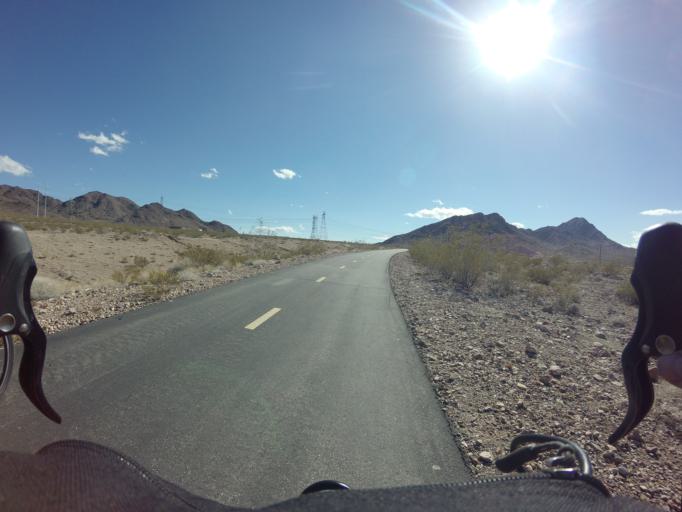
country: US
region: Nevada
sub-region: Clark County
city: Henderson
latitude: 35.9895
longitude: -114.9203
